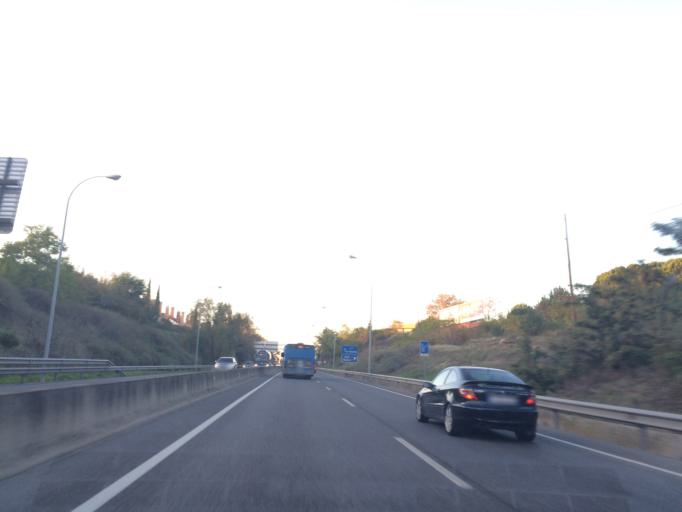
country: ES
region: Madrid
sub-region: Provincia de Madrid
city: Moncloa-Aravaca
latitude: 40.4574
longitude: -3.7686
